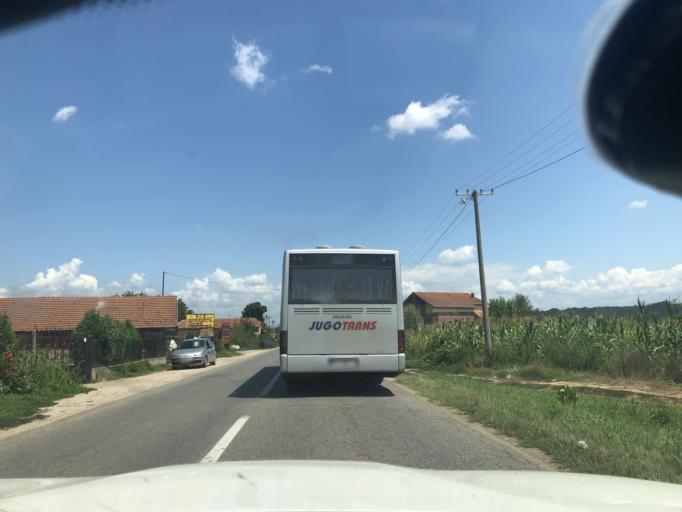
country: RS
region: Central Serbia
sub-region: Jablanicki Okrug
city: Leskovac
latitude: 42.9697
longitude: 21.8767
